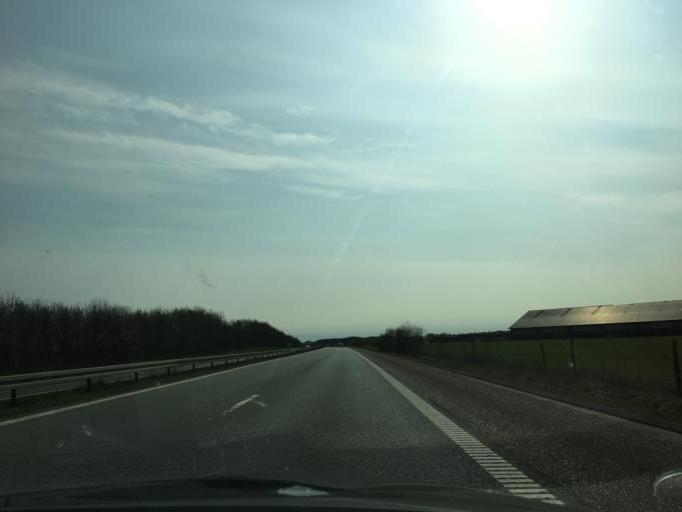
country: DK
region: South Denmark
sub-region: Vejen Kommune
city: Holsted
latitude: 55.5137
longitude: 8.9505
